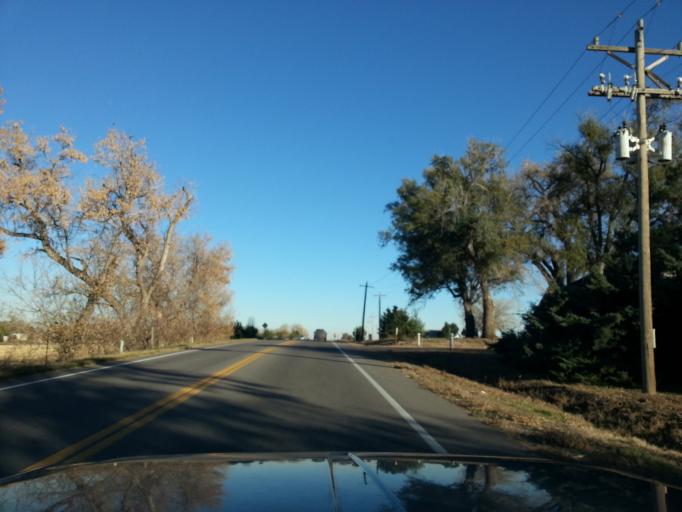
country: US
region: Colorado
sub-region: Larimer County
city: Loveland
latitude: 40.3783
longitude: -105.0173
